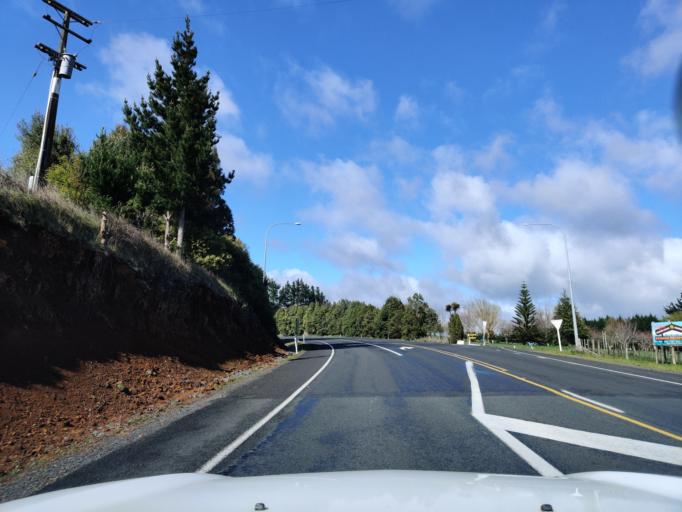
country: NZ
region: Waikato
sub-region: Otorohanga District
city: Otorohanga
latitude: -38.0645
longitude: 175.1560
